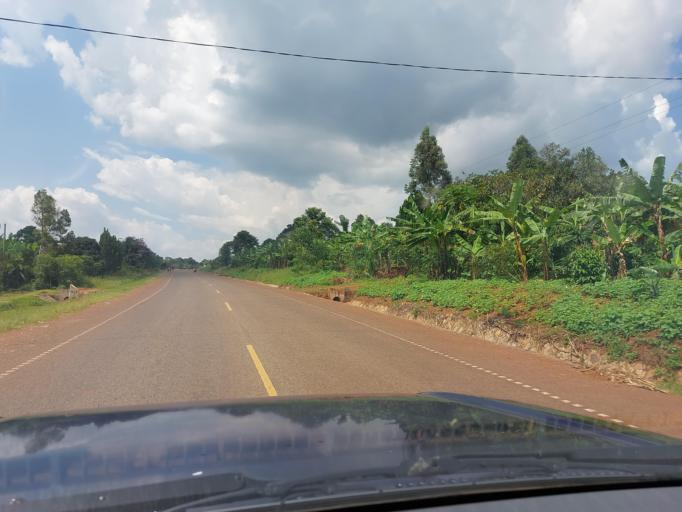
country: UG
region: Central Region
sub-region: Buikwe District
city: Buikwe
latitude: 0.3242
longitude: 33.1144
